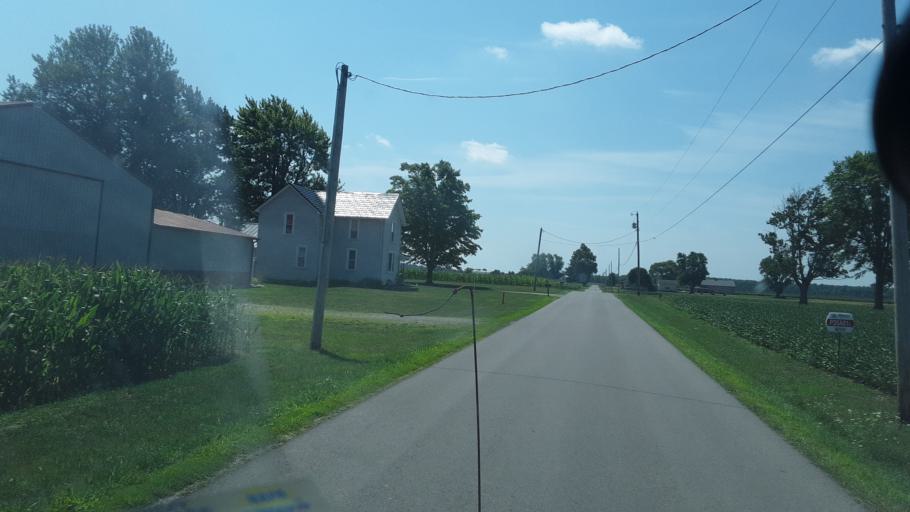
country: US
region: Ohio
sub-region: Hancock County
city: Findlay
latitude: 40.9991
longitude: -83.5161
